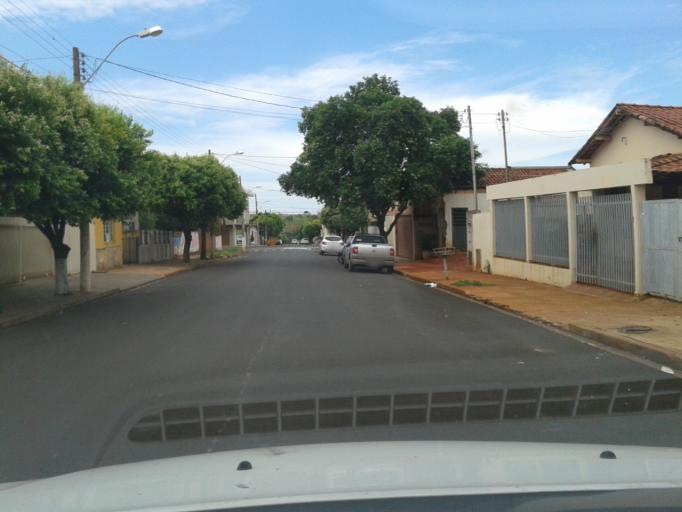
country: BR
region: Minas Gerais
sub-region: Iturama
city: Iturama
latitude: -19.7329
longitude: -50.1970
